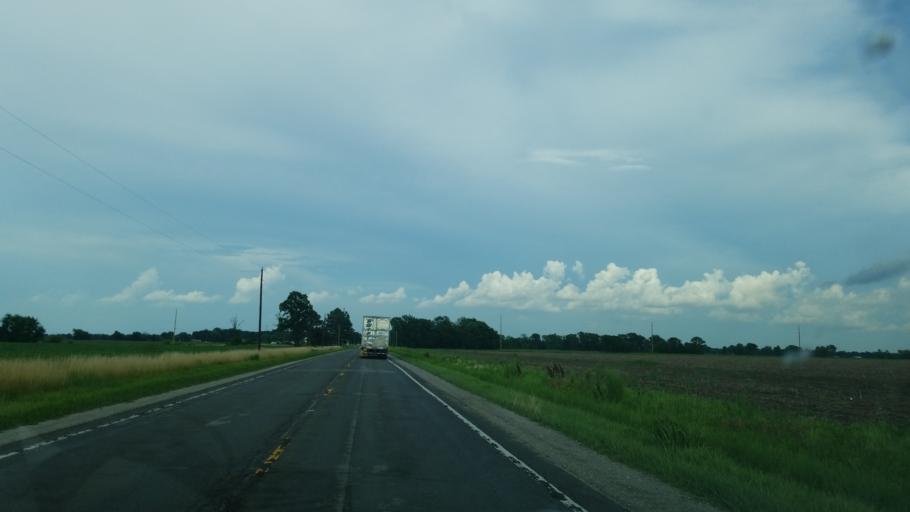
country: US
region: Illinois
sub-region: Marion County
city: Sandoval
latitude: 38.6165
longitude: -89.1446
